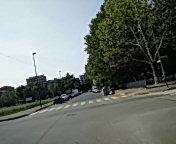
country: IT
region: Piedmont
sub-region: Provincia di Torino
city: Nichelino
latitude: 45.0264
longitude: 7.6433
